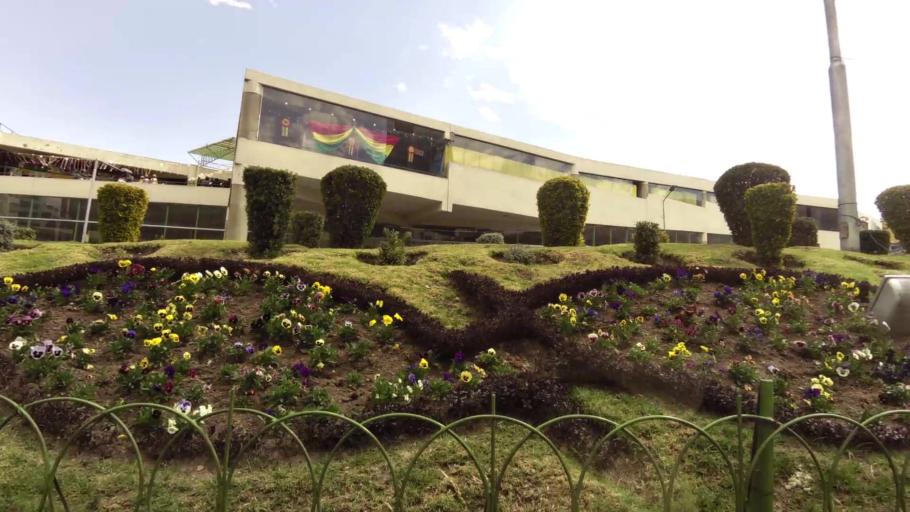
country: BO
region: La Paz
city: La Paz
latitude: -16.4948
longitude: -68.1369
